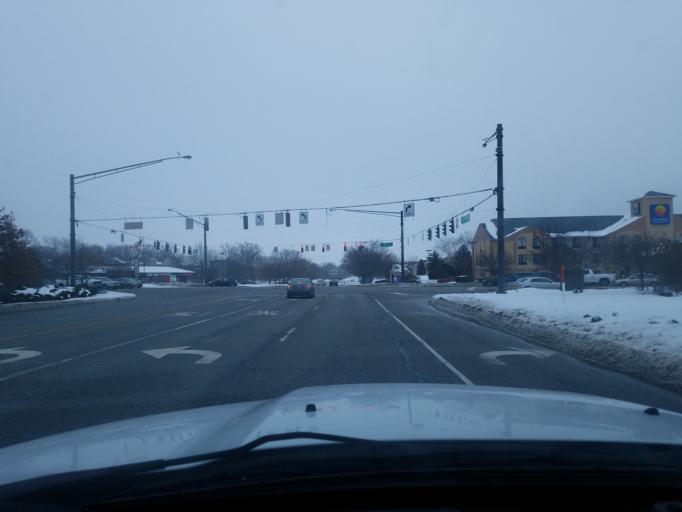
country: US
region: Indiana
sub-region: Saint Joseph County
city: Georgetown
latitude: 41.7127
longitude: -86.1796
